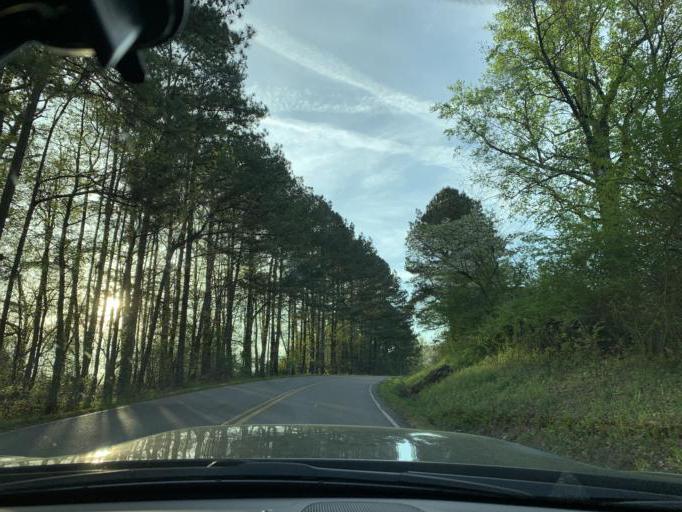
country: US
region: Georgia
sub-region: Forsyth County
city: Cumming
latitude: 34.2587
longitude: -84.1481
